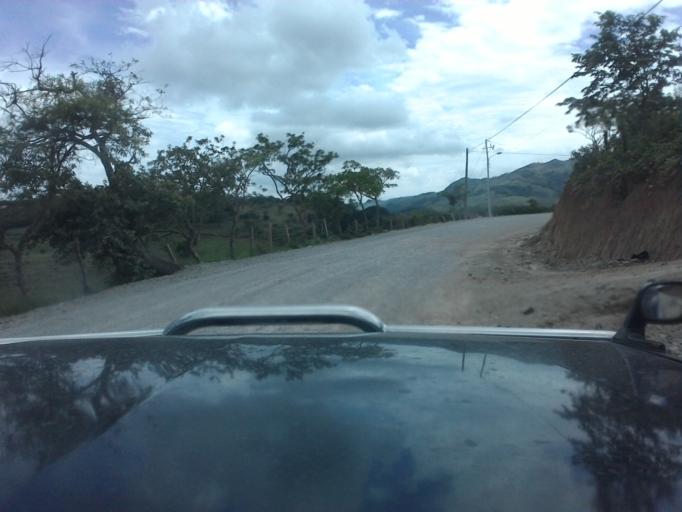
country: CR
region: Guanacaste
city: Juntas
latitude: 10.2780
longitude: -84.8432
